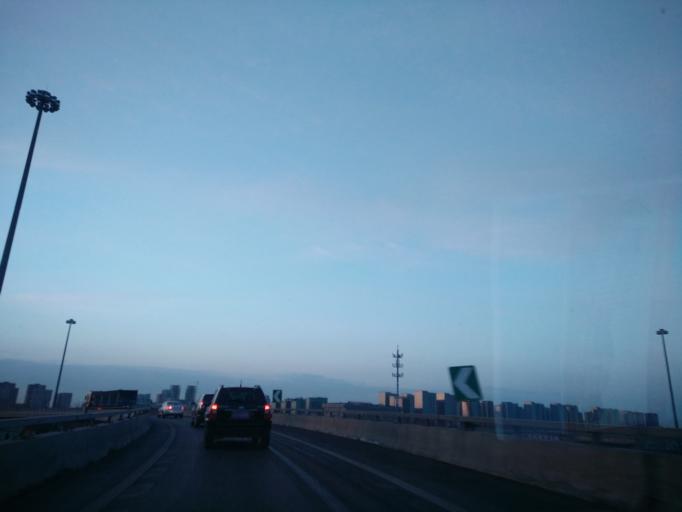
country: CN
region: Beijing
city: Jiugong
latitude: 39.8183
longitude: 116.4965
